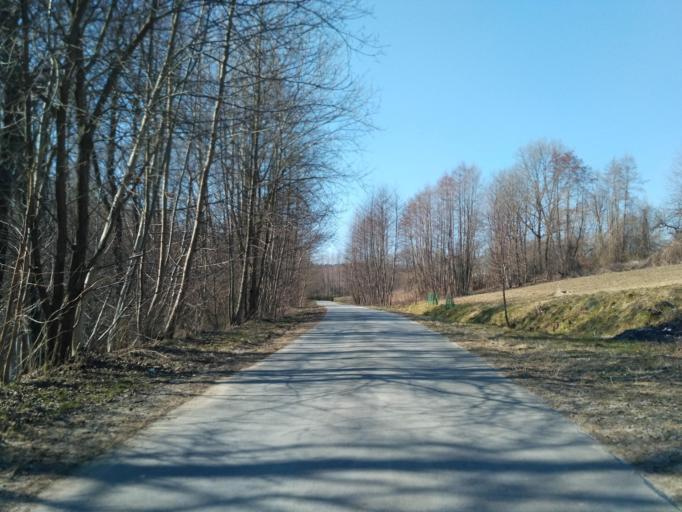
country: PL
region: Subcarpathian Voivodeship
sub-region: Powiat rzeszowski
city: Niechobrz
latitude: 49.9717
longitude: 21.8854
